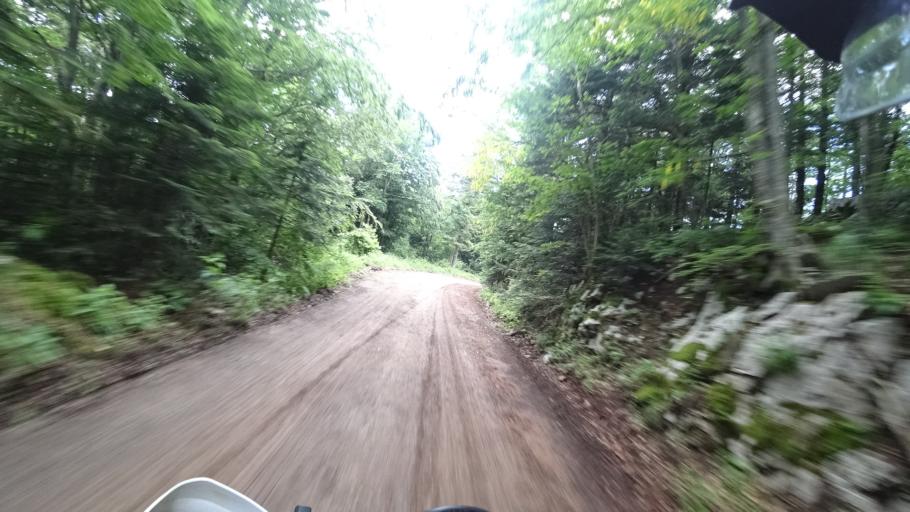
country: HR
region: Primorsko-Goranska
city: Bribir
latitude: 45.2257
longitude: 14.7565
